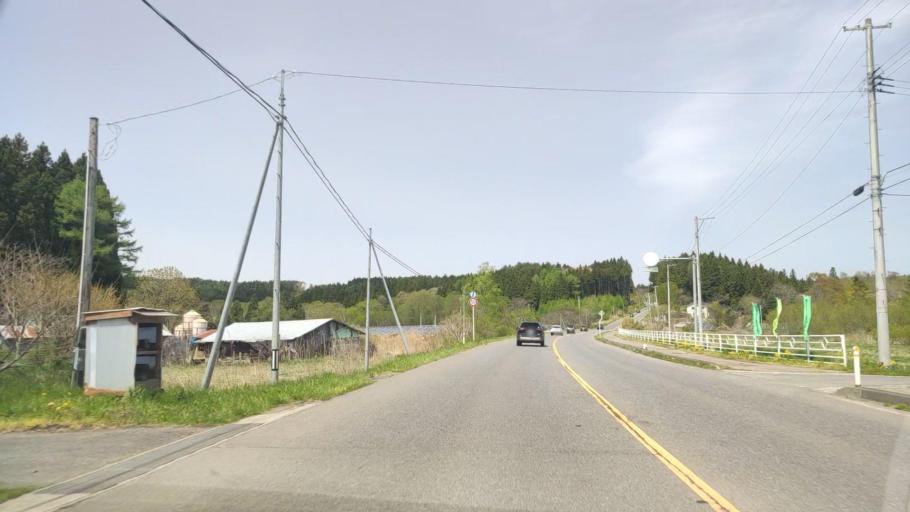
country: JP
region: Aomori
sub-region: Misawa Shi
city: Inuotose
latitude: 40.5619
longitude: 141.3830
